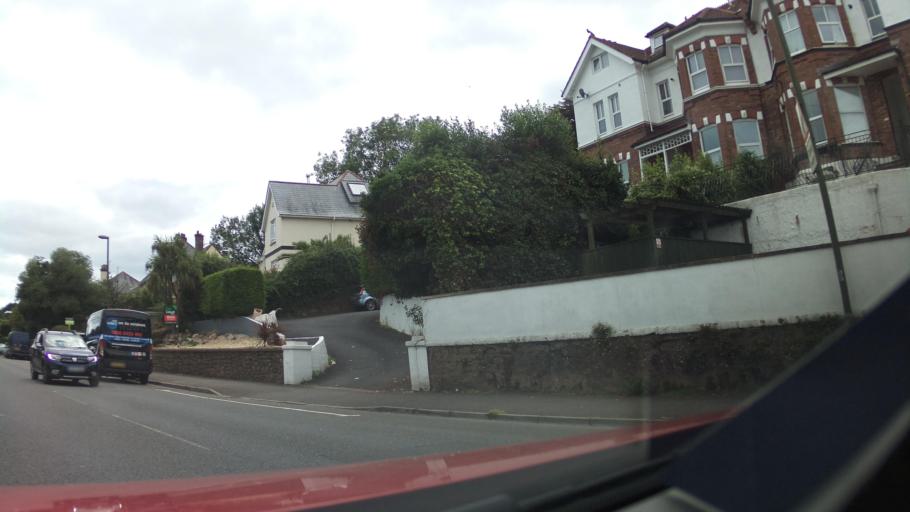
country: GB
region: England
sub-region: Borough of Torbay
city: Paignton
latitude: 50.4287
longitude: -3.5652
